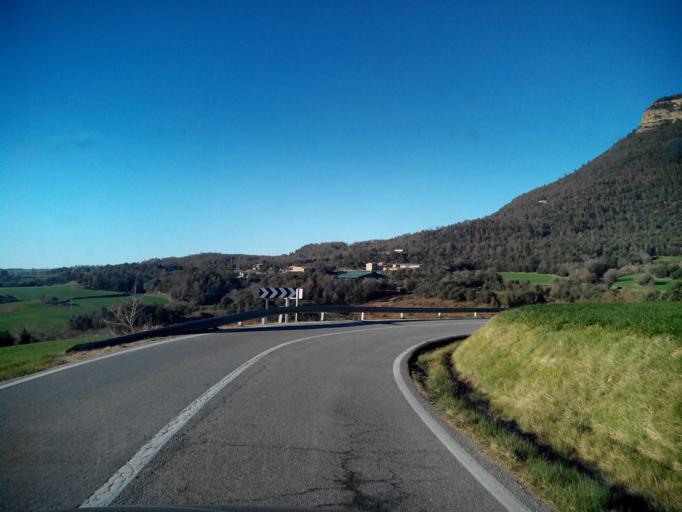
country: ES
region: Catalonia
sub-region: Provincia de Barcelona
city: Avia
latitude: 42.0666
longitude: 1.8019
